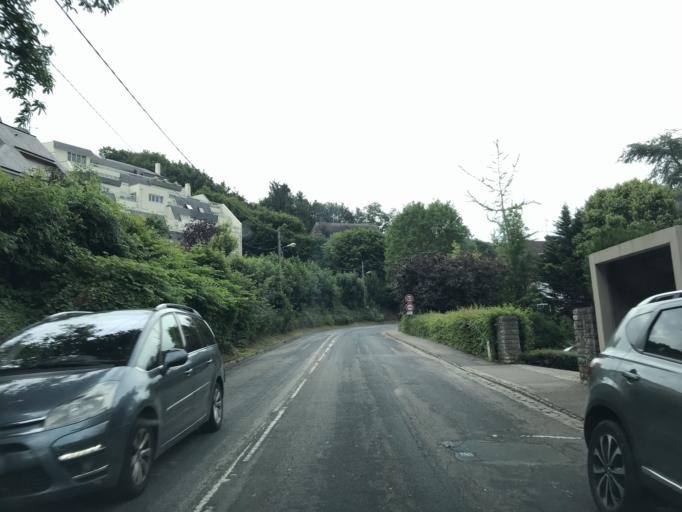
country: FR
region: Haute-Normandie
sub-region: Departement de la Seine-Maritime
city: Mont-Saint-Aignan
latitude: 49.4568
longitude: 1.0841
